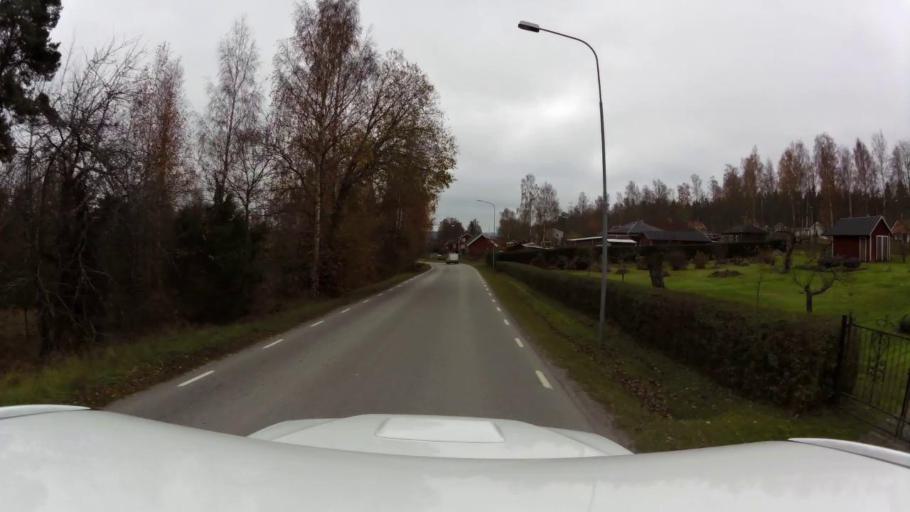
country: SE
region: OEstergoetland
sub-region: Kinda Kommun
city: Rimforsa
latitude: 58.1423
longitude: 15.6706
